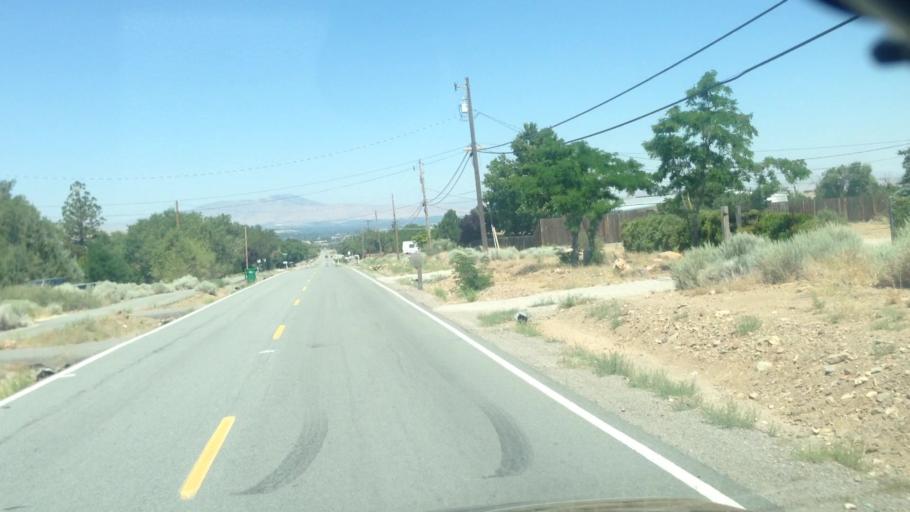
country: US
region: Nevada
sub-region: Storey County
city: Virginia City
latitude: 39.3786
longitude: -119.7191
